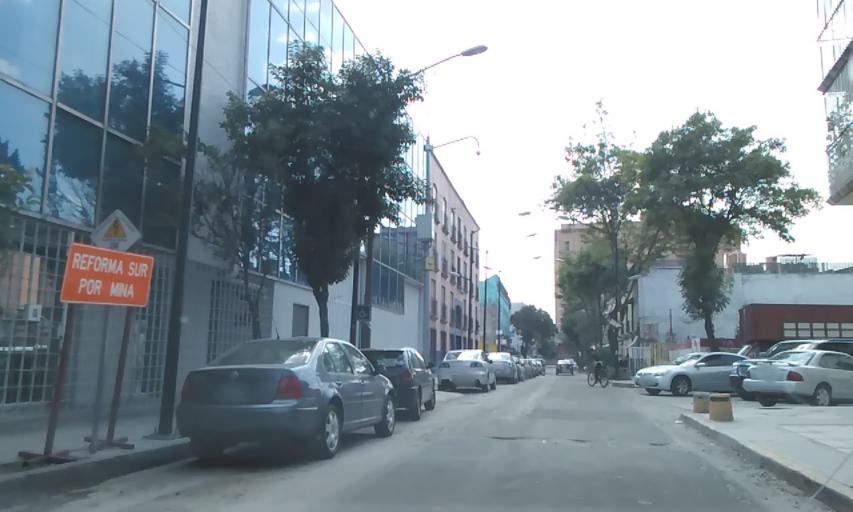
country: MX
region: Mexico City
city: Cuauhtemoc
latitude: 19.4388
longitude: -99.1420
